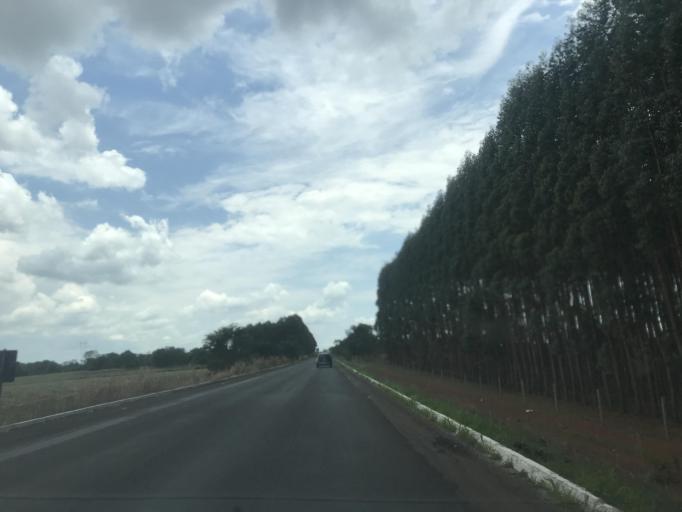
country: BR
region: Goias
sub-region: Vianopolis
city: Vianopolis
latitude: -16.9336
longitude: -48.5575
